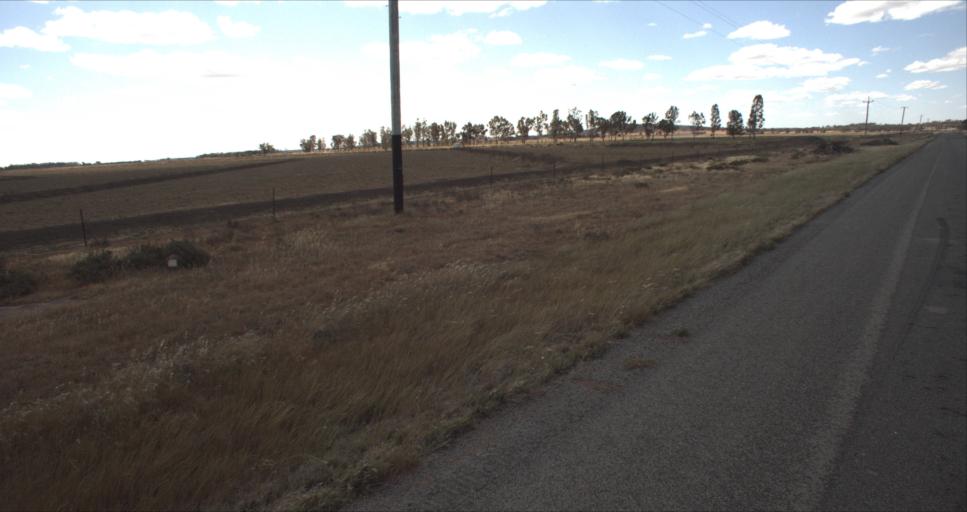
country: AU
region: New South Wales
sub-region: Leeton
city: Leeton
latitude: -34.4428
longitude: 146.2561
